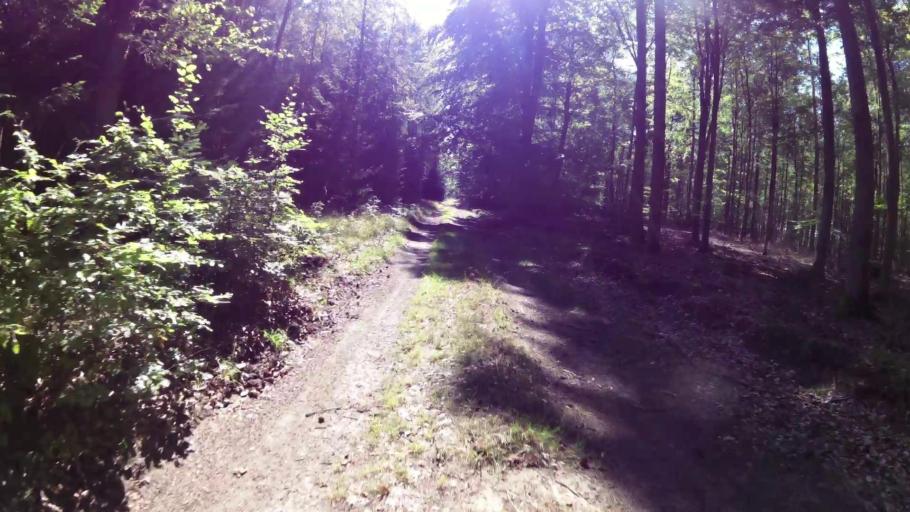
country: PL
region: West Pomeranian Voivodeship
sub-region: Powiat drawski
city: Czaplinek
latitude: 53.4540
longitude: 16.2179
